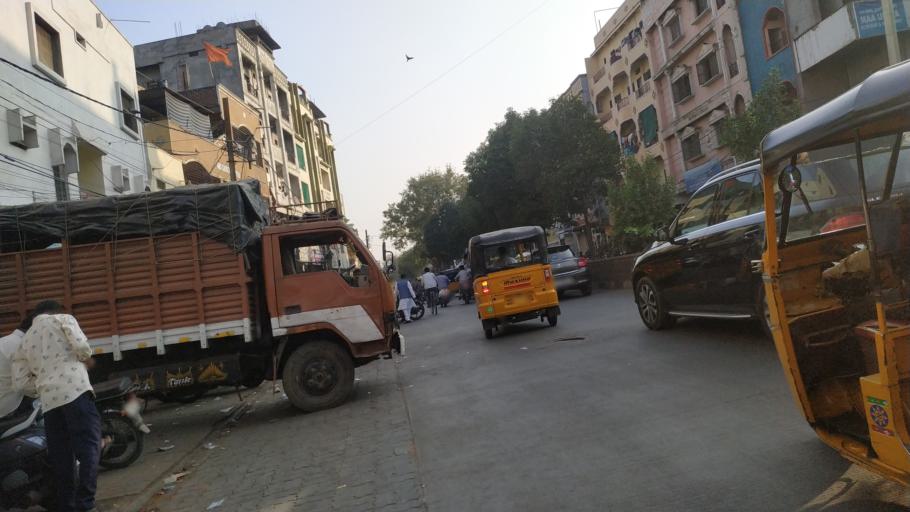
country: IN
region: Telangana
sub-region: Rangareddi
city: Kukatpalli
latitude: 17.4465
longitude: 78.4491
